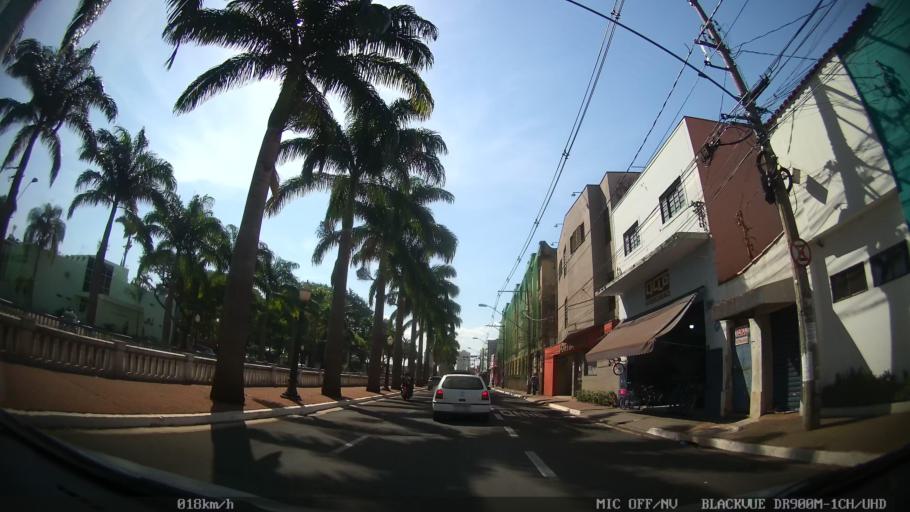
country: BR
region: Sao Paulo
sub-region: Ribeirao Preto
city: Ribeirao Preto
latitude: -21.1734
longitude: -47.8132
